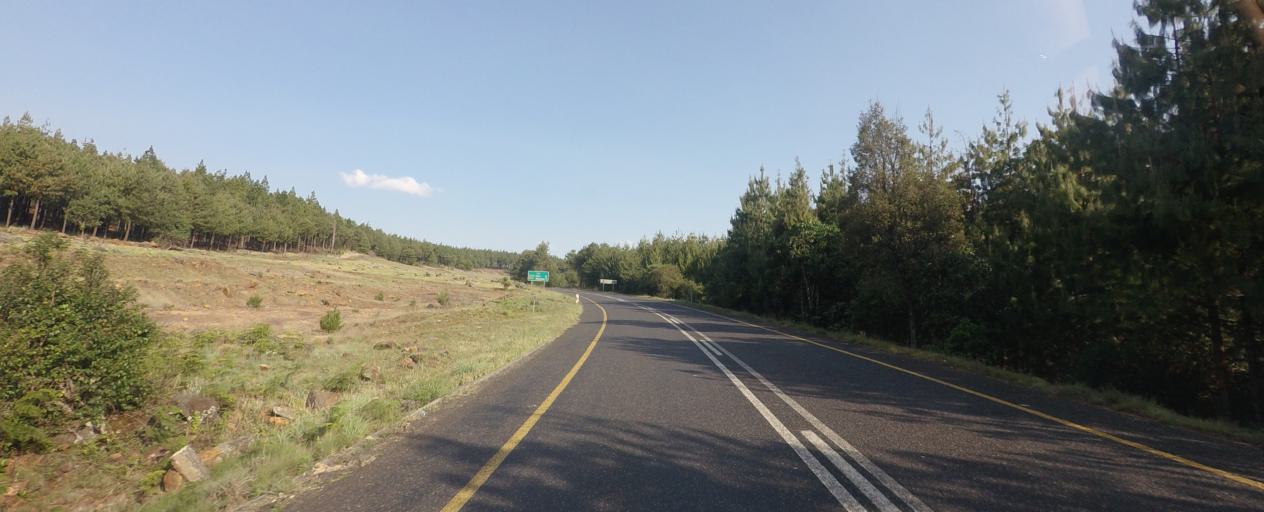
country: ZA
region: Mpumalanga
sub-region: Ehlanzeni District
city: Lydenburg
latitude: -25.1698
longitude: 30.6491
